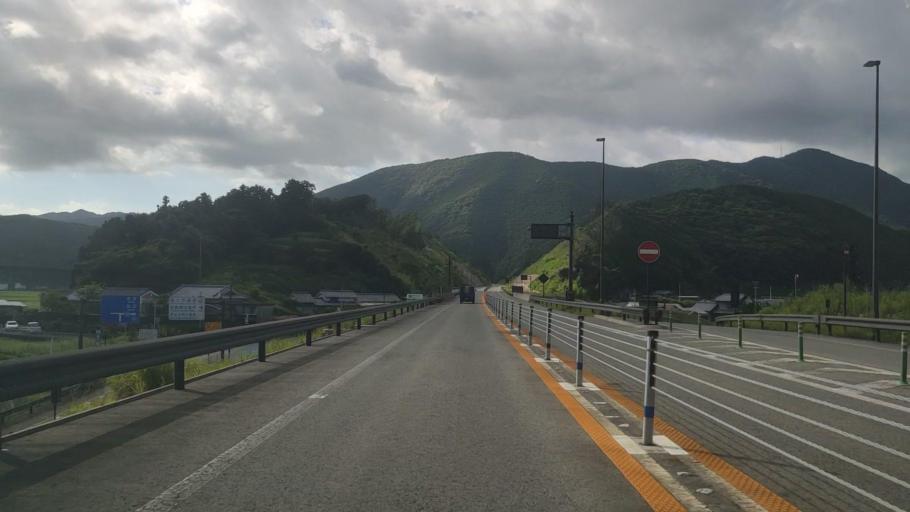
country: JP
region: Wakayama
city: Tanabe
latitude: 33.5552
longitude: 135.5101
